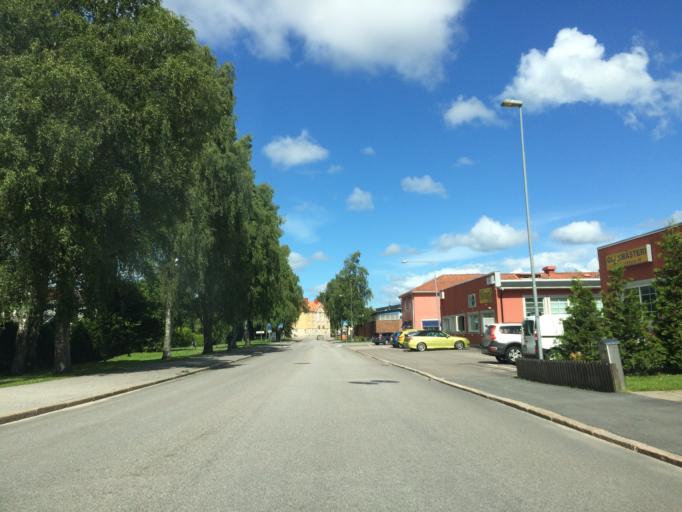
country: SE
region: Vaestra Goetaland
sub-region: Trollhattan
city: Trollhattan
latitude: 58.2830
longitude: 12.3013
